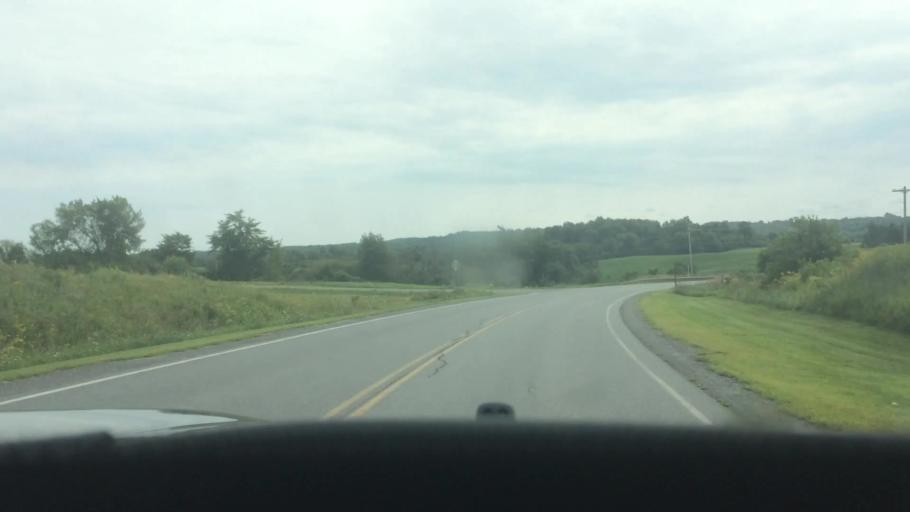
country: US
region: New York
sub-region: St. Lawrence County
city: Canton
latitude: 44.4964
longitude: -75.2537
